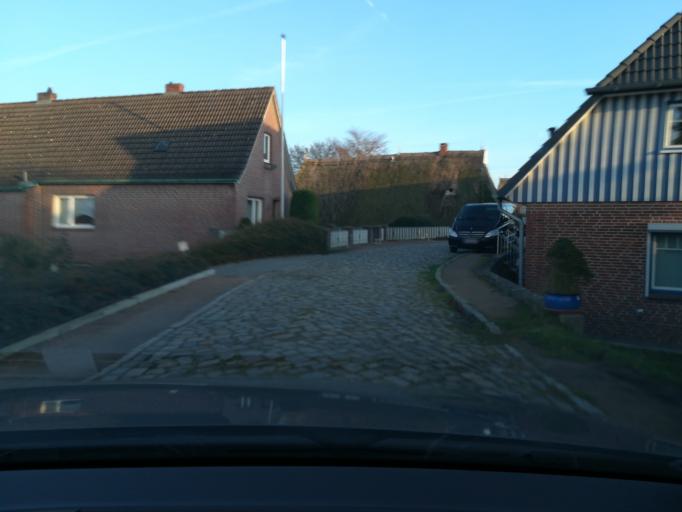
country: DE
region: Lower Saxony
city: Winsen
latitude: 53.3984
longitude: 10.2265
